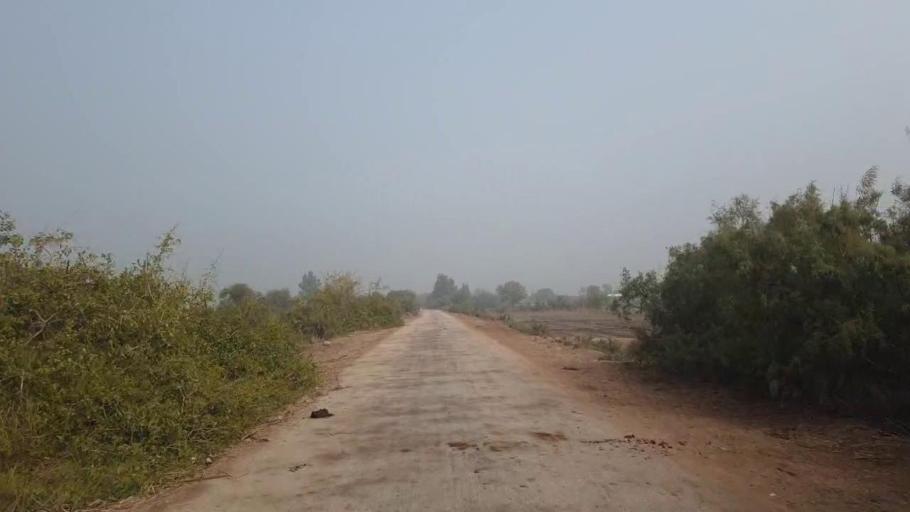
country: PK
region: Sindh
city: Bhit Shah
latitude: 25.8169
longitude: 68.5619
